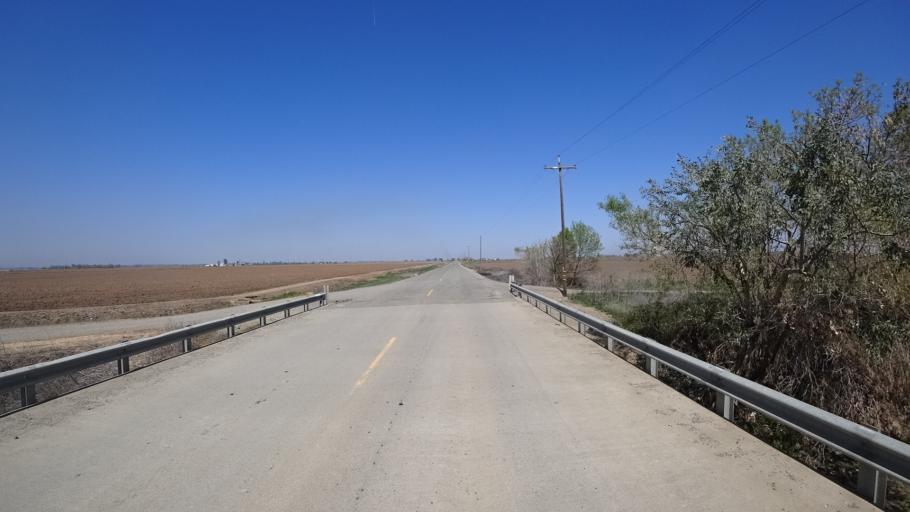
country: US
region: California
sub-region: Glenn County
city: Willows
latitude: 39.5050
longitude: -122.1366
